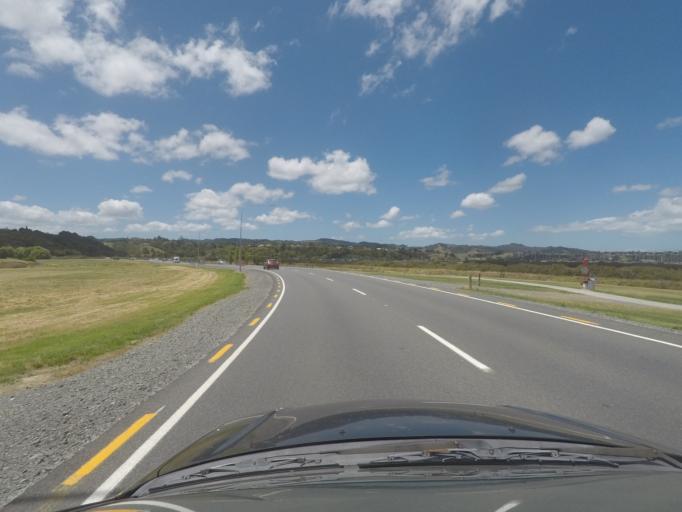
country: NZ
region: Northland
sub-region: Whangarei
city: Whangarei
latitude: -35.7350
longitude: 174.3404
